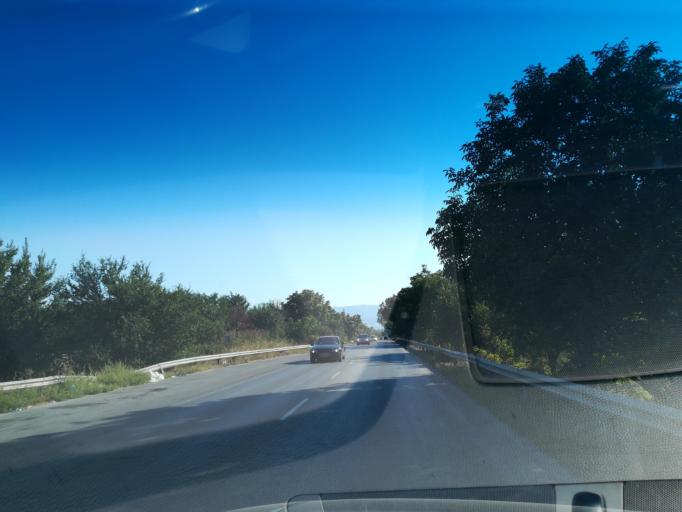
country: BG
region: Plovdiv
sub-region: Obshtina Plovdiv
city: Plovdiv
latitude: 42.1686
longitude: 24.8172
